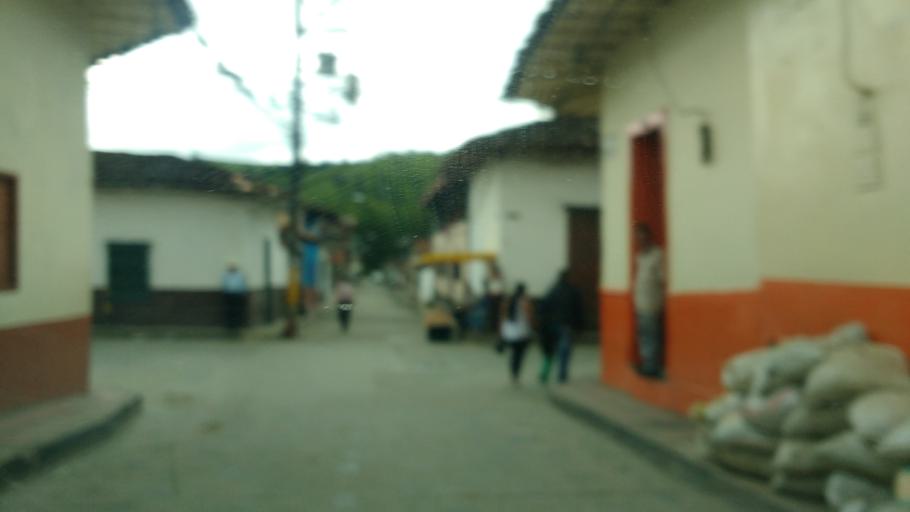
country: CO
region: Antioquia
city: Concepcion
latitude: 6.3939
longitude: -75.2588
